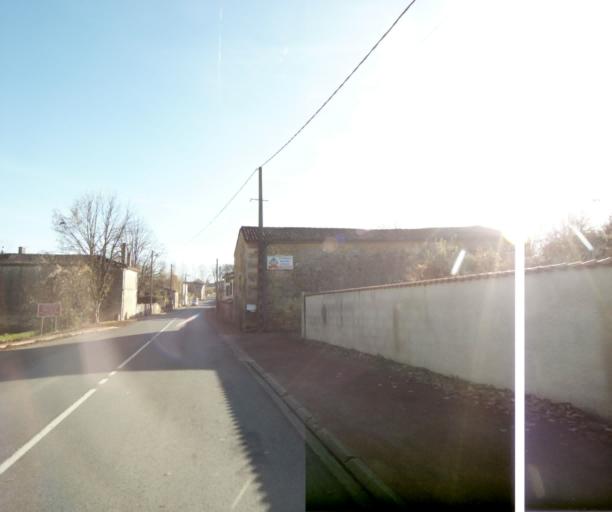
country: FR
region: Poitou-Charentes
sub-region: Departement de la Charente-Maritime
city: Burie
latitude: 45.7906
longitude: -0.4368
